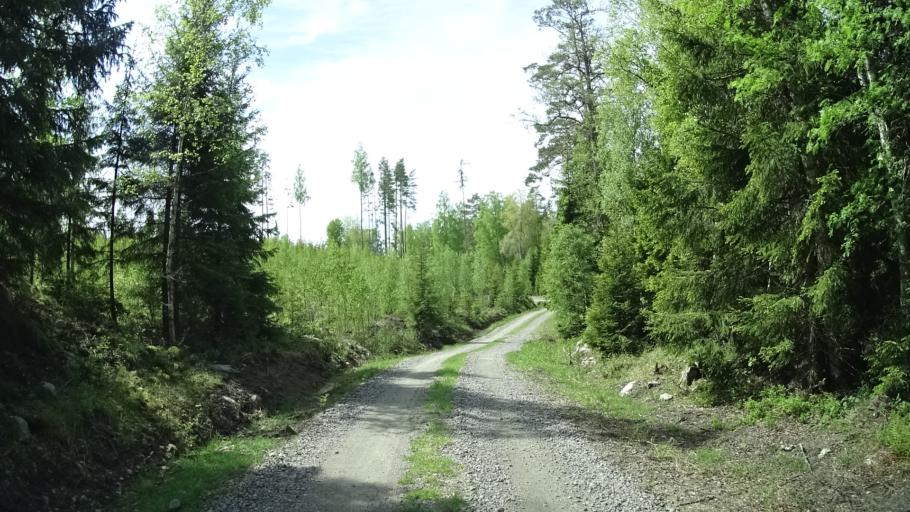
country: SE
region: OEstergoetland
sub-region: Finspangs Kommun
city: Finspang
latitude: 58.8044
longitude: 15.8404
